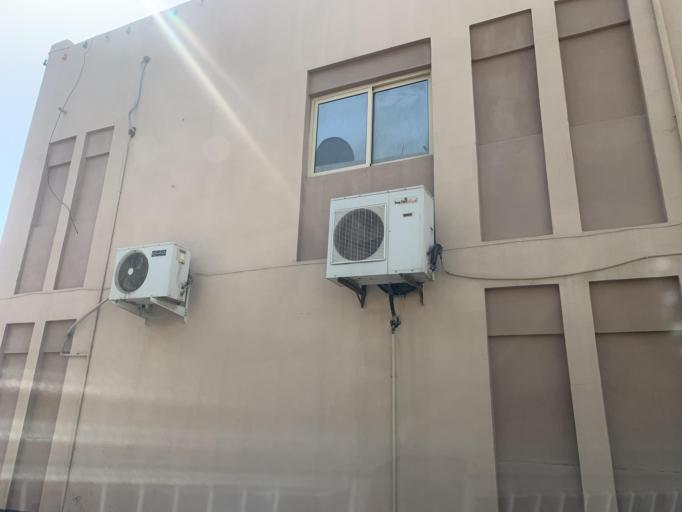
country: BH
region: Manama
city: Jidd Hafs
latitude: 26.2044
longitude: 50.5308
